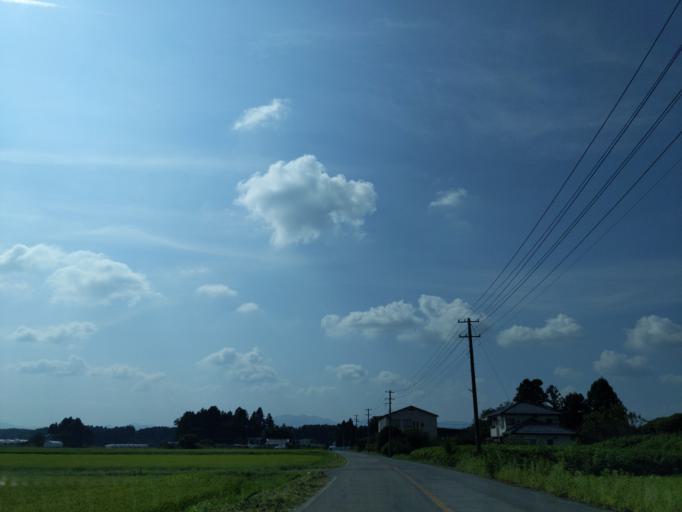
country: JP
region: Fukushima
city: Sukagawa
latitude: 37.3083
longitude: 140.3238
